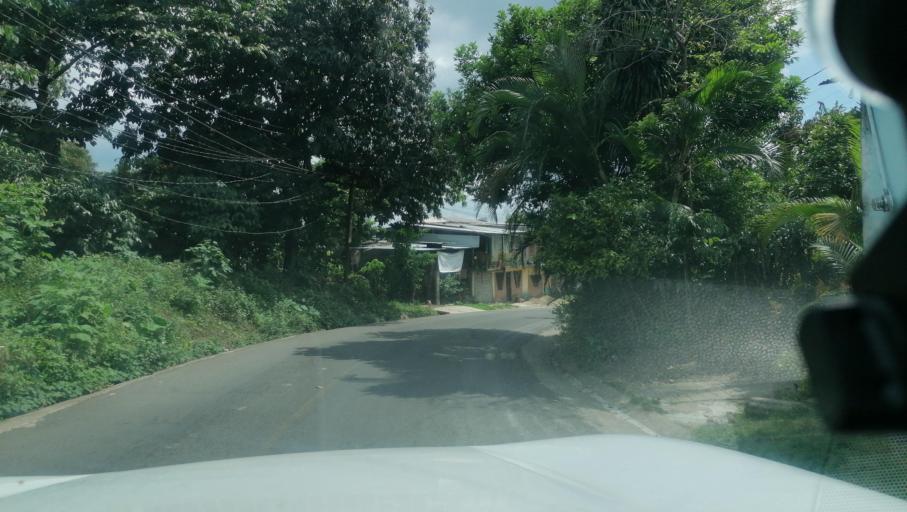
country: MX
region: Chiapas
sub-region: Cacahoatan
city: Benito Juarez
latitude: 15.0366
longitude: -92.1540
